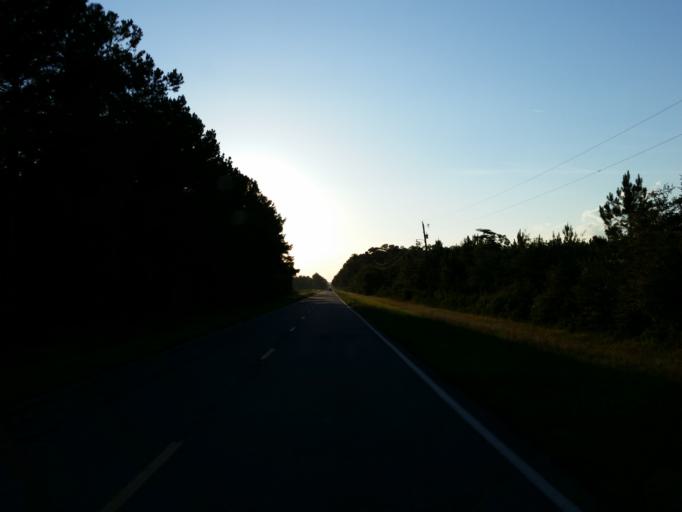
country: US
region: Georgia
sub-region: Lanier County
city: Lakeland
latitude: 31.1690
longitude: -83.1026
